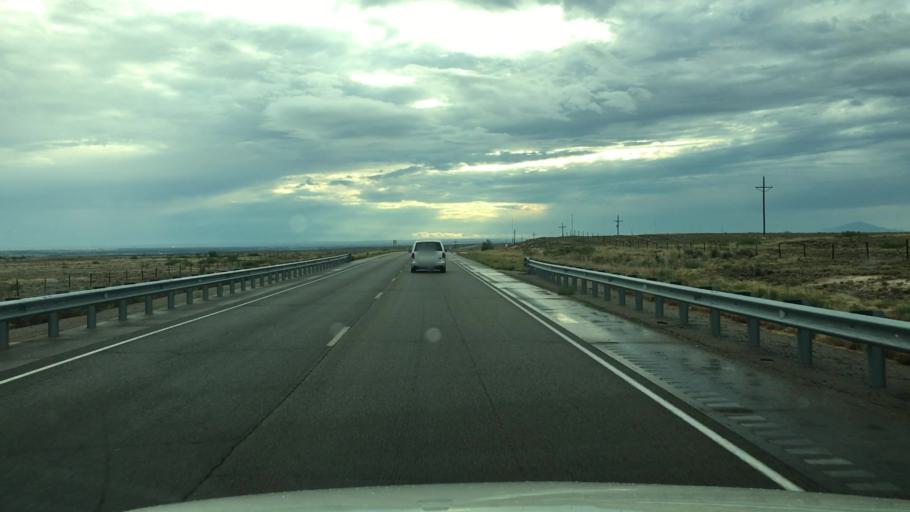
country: US
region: New Mexico
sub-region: Chaves County
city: Roswell
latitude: 33.4003
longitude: -104.3406
